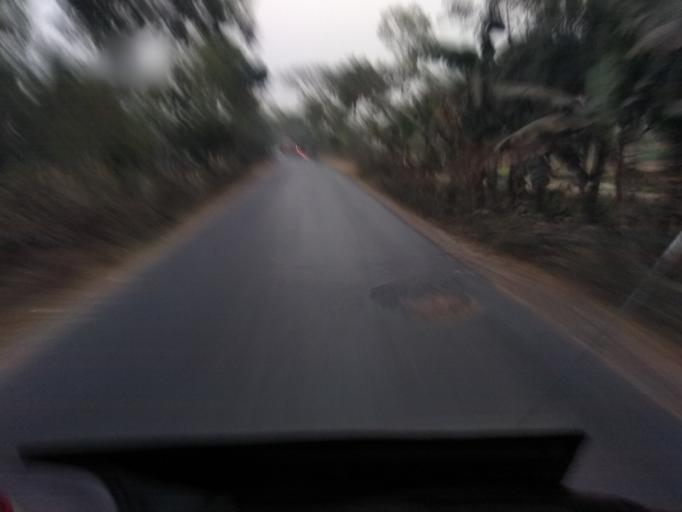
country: BD
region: Rajshahi
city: Bogra
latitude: 24.7339
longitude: 89.3267
